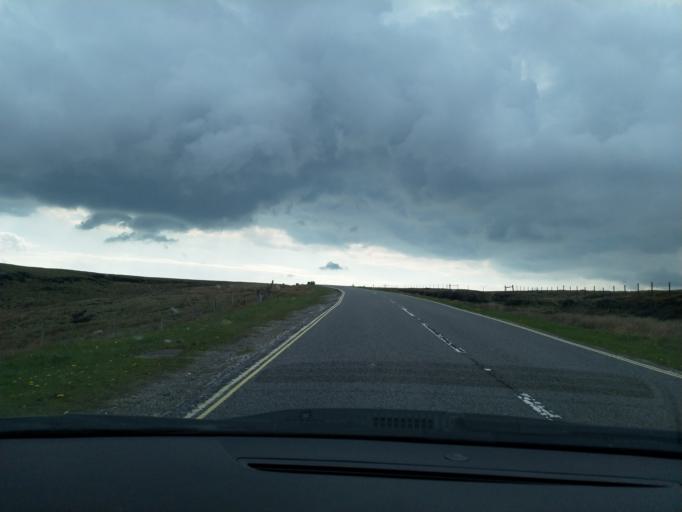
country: GB
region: England
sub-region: Derbyshire
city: High Peak
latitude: 53.4328
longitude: -1.8611
